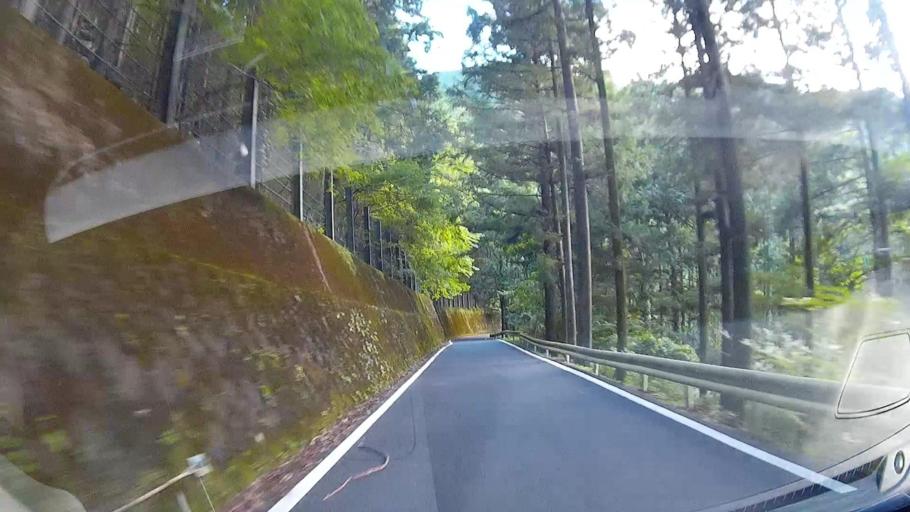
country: JP
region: Shizuoka
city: Shizuoka-shi
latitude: 35.1365
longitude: 138.2749
